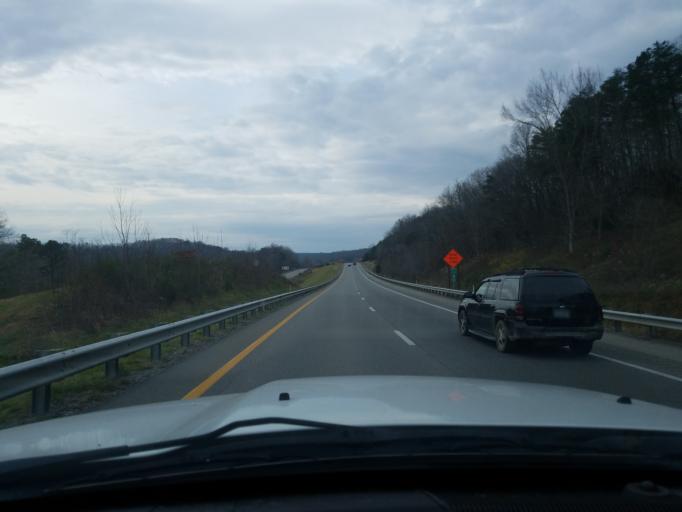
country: US
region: Kentucky
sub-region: Carter County
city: Olive Hill
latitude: 38.3226
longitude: -83.1435
